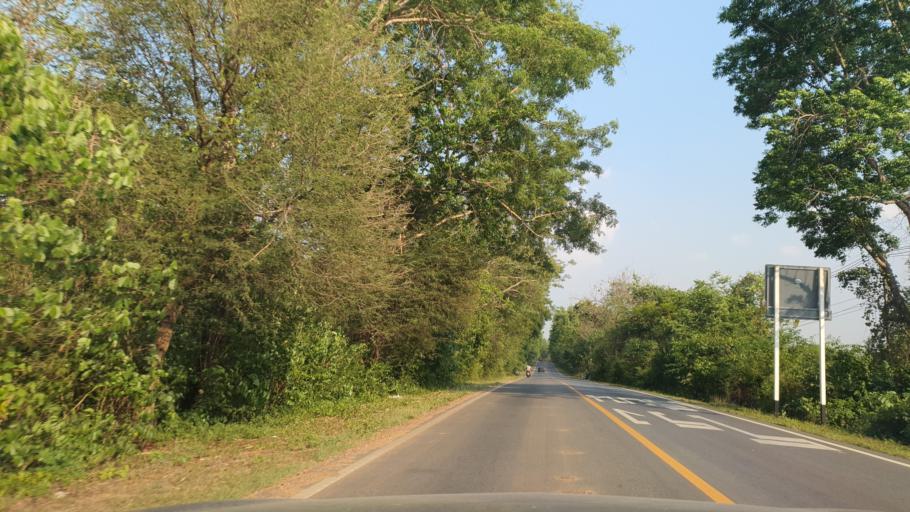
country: TH
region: Kanchanaburi
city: Sai Yok
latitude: 14.2059
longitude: 99.2487
